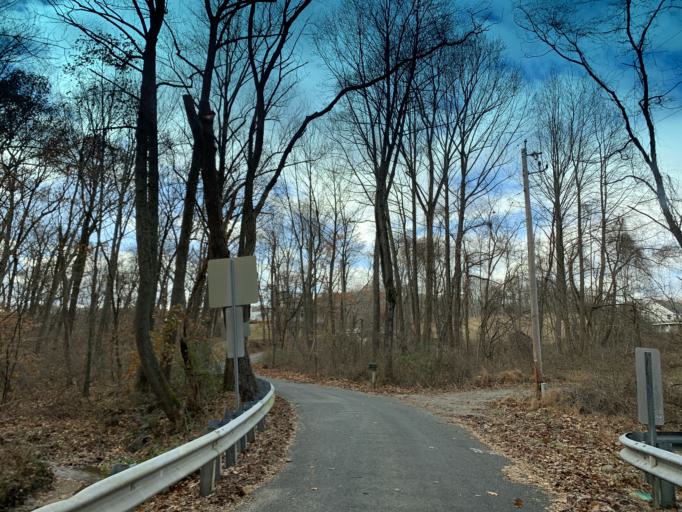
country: US
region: Maryland
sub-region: Harford County
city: Bel Air North
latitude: 39.5925
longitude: -76.4127
